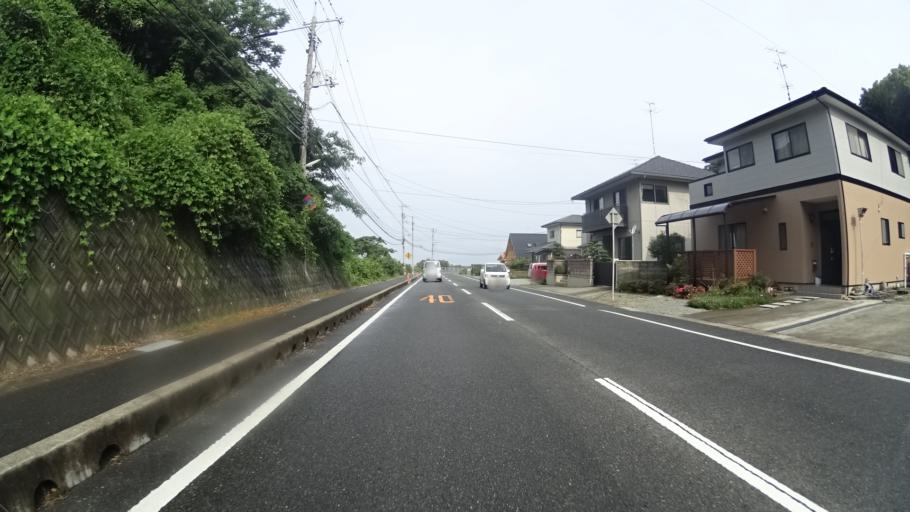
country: JP
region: Yamaguchi
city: Shimonoseki
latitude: 34.0839
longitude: 130.8850
